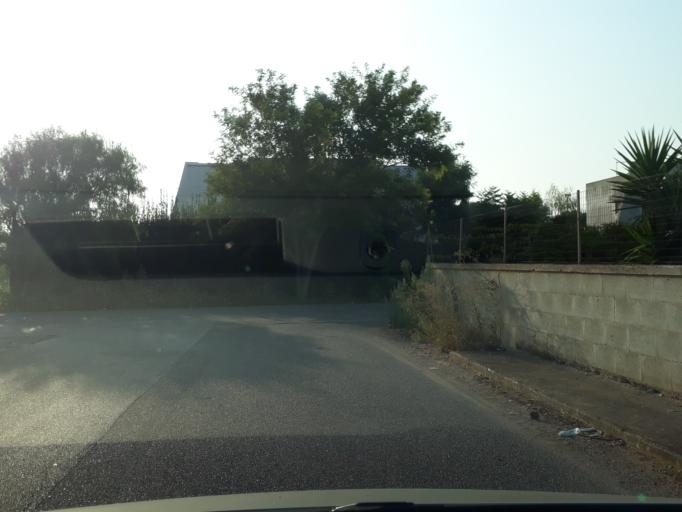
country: IT
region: Apulia
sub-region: Provincia di Brindisi
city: Carovigno
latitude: 40.7531
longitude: 17.7077
